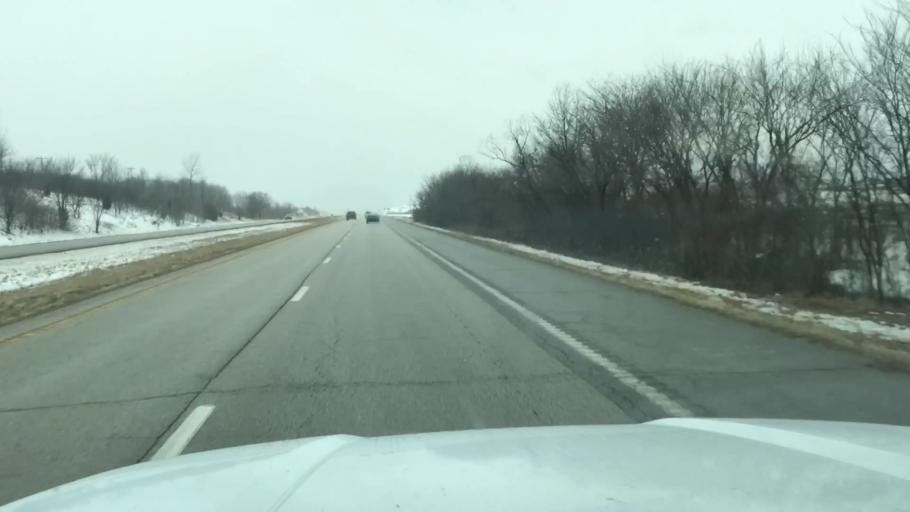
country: US
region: Missouri
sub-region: Clinton County
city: Gower
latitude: 39.7477
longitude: -94.6763
